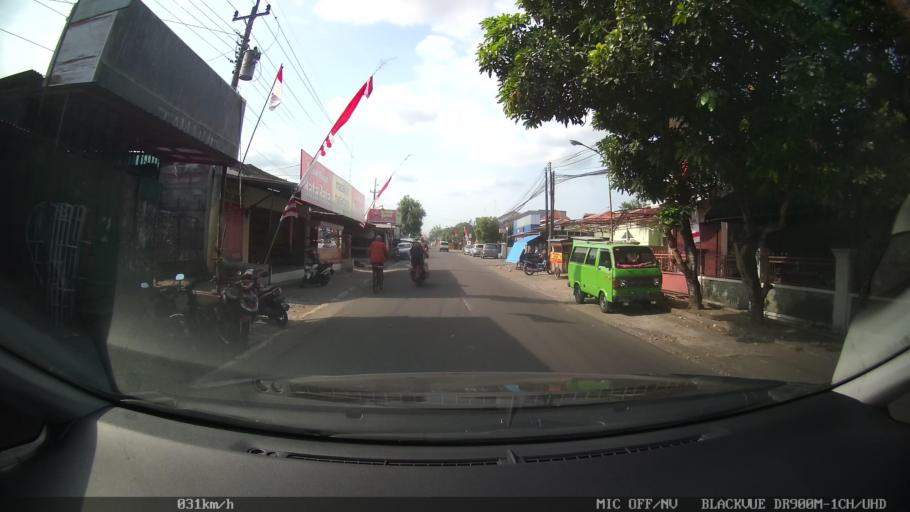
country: ID
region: Daerah Istimewa Yogyakarta
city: Depok
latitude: -7.7455
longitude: 110.4500
